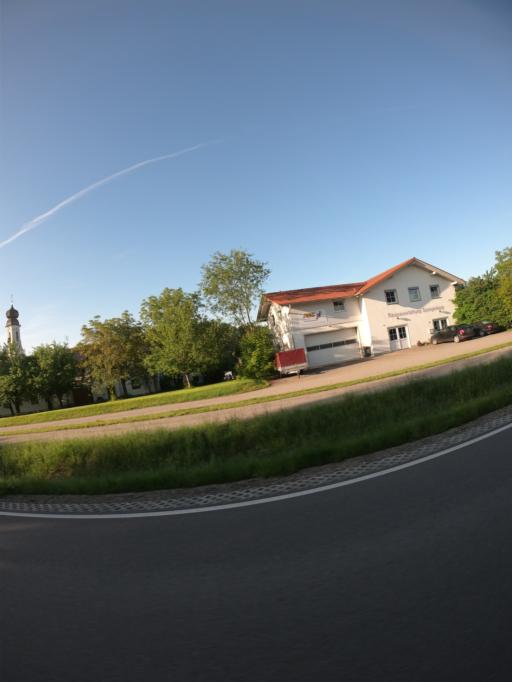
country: DE
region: Bavaria
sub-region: Upper Bavaria
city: Inning am Holz
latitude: 48.3373
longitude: 12.0620
